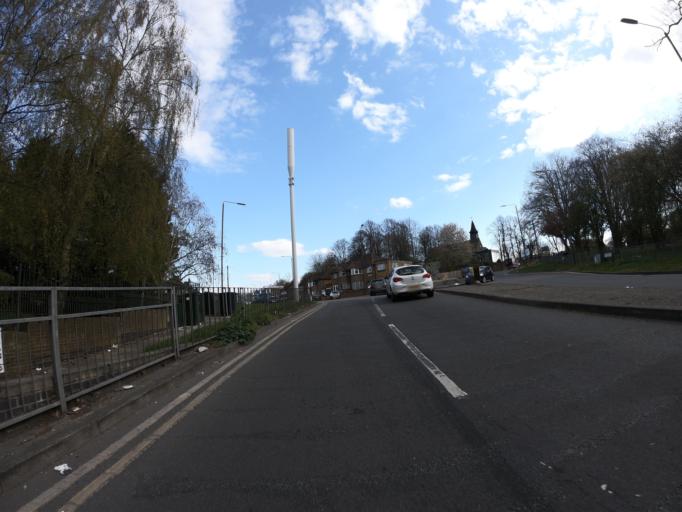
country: GB
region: England
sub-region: Greater London
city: Welling
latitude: 51.4733
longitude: 0.1117
